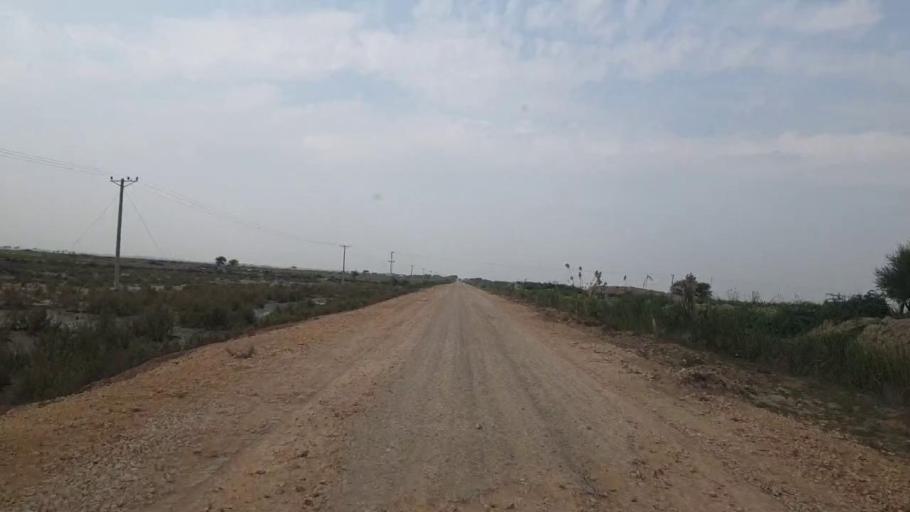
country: PK
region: Sindh
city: Kario
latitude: 24.6152
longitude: 68.5878
